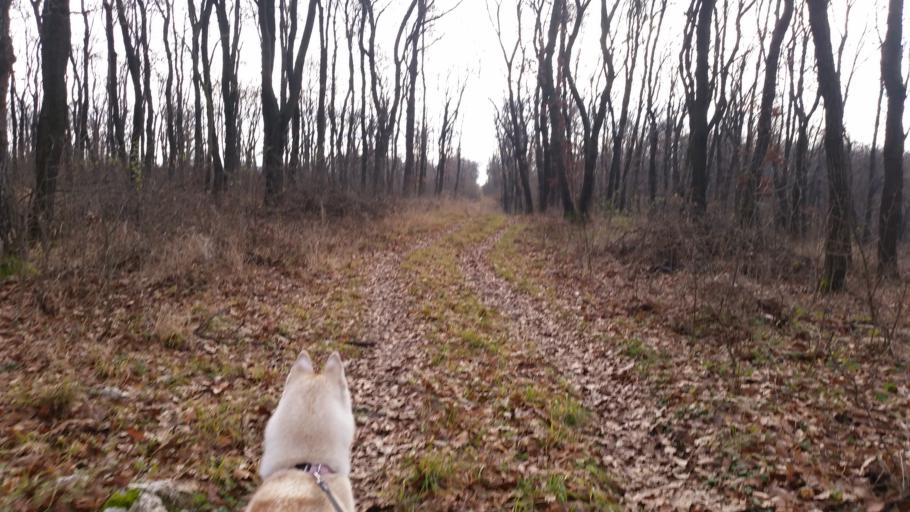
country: HU
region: Pest
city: Telki
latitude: 47.5739
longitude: 18.8294
